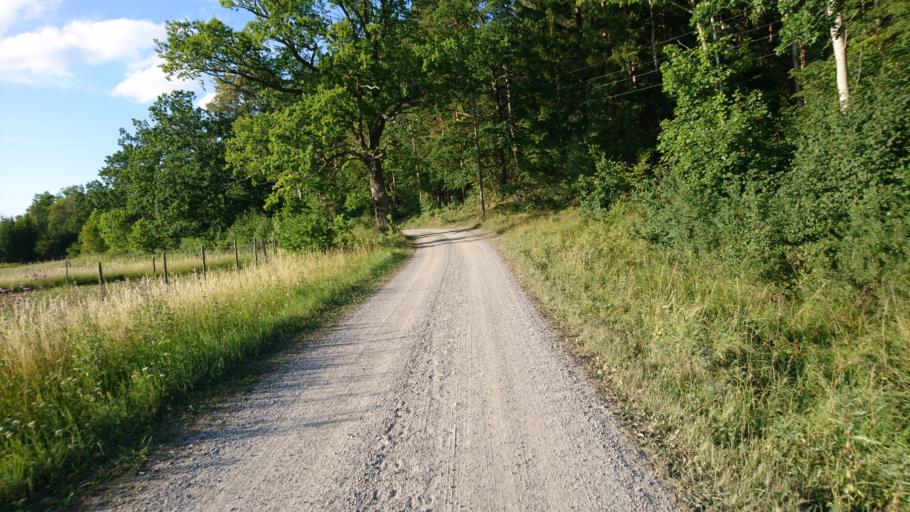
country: SE
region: Soedermanland
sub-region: Strangnas Kommun
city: Stallarholmen
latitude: 59.3858
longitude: 17.3081
